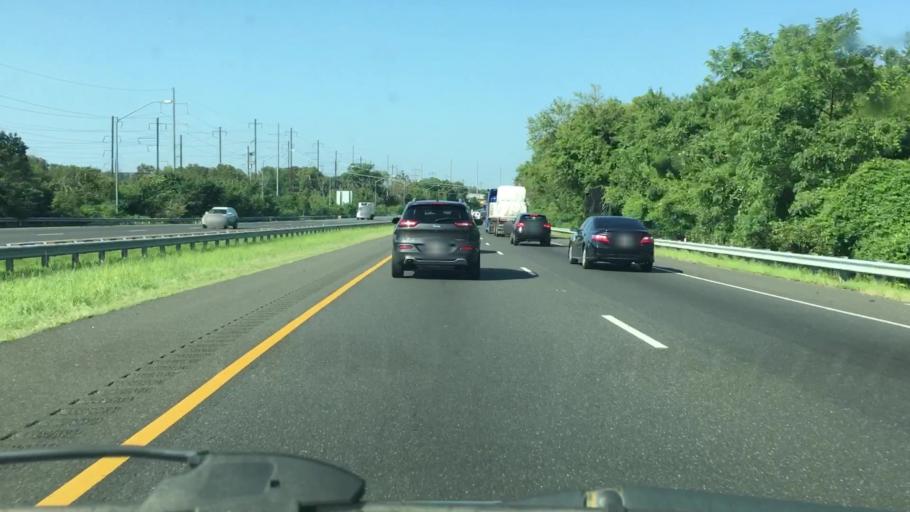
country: US
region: Maryland
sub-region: Prince George's County
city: Cheverly
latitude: 38.9206
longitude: -76.9083
